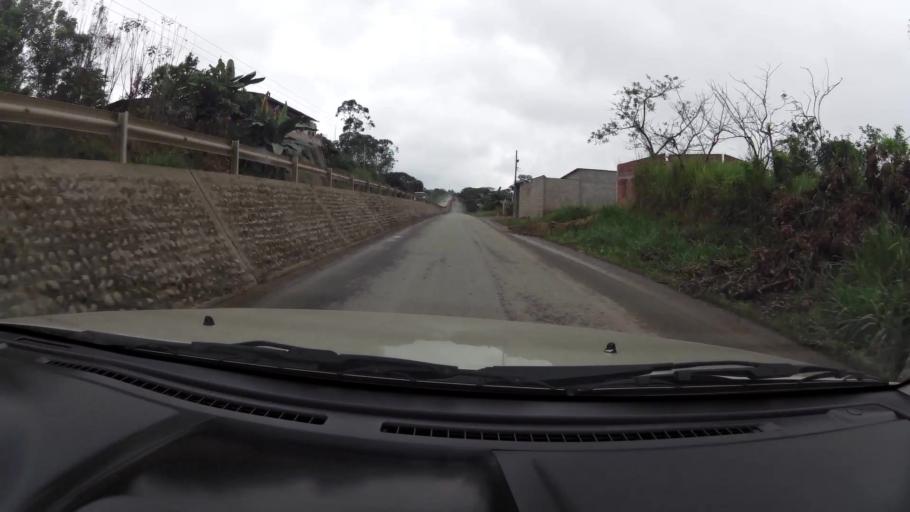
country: EC
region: El Oro
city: Pasaje
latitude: -3.3325
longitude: -79.7857
